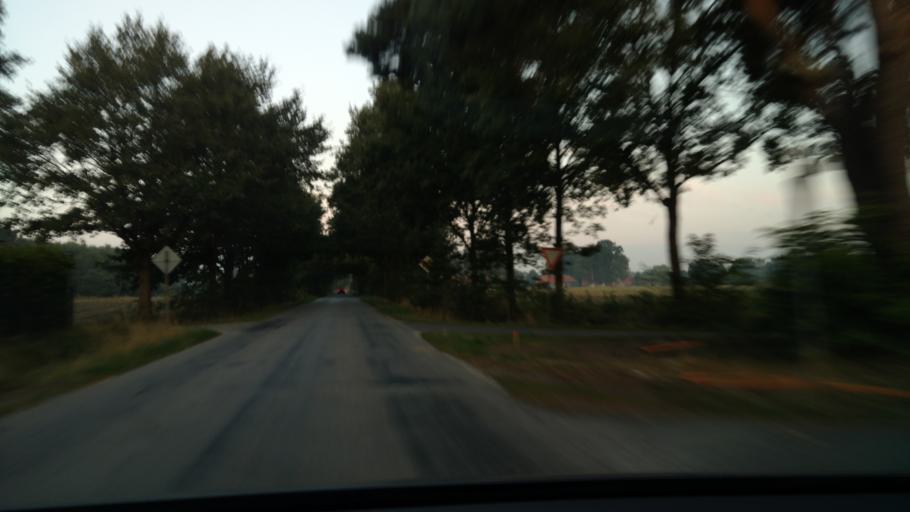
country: DE
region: North Rhine-Westphalia
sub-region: Regierungsbezirk Munster
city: Klein Reken
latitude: 51.8548
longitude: 7.0637
